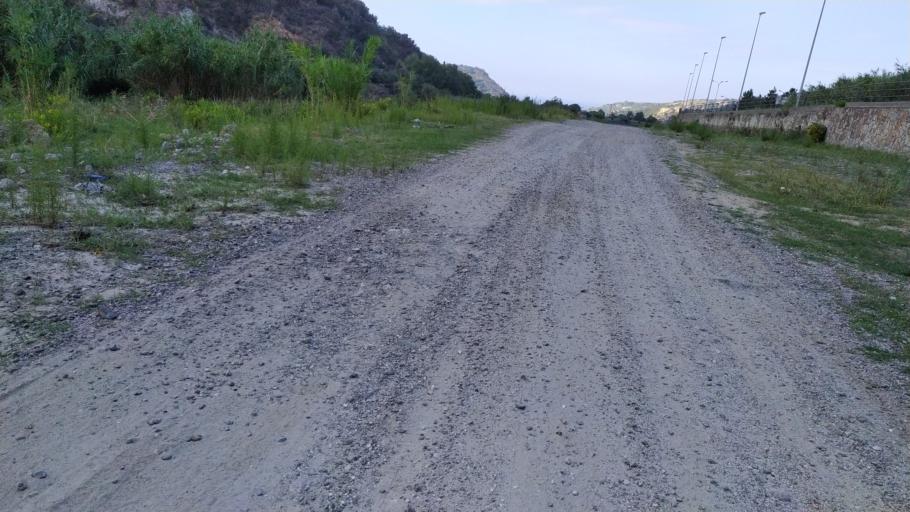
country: IT
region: Sicily
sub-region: Messina
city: Saponara
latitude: 38.1973
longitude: 15.4299
